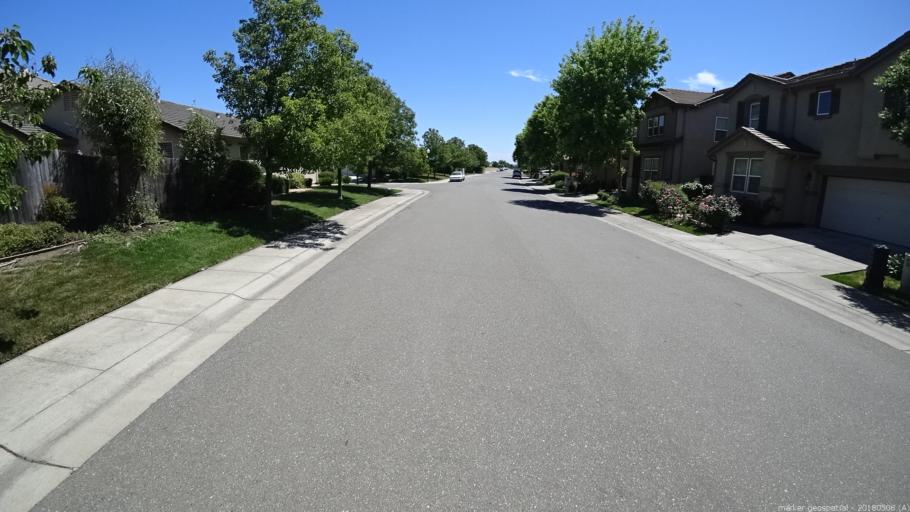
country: US
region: California
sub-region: Sacramento County
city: Elverta
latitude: 38.6786
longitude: -121.5389
